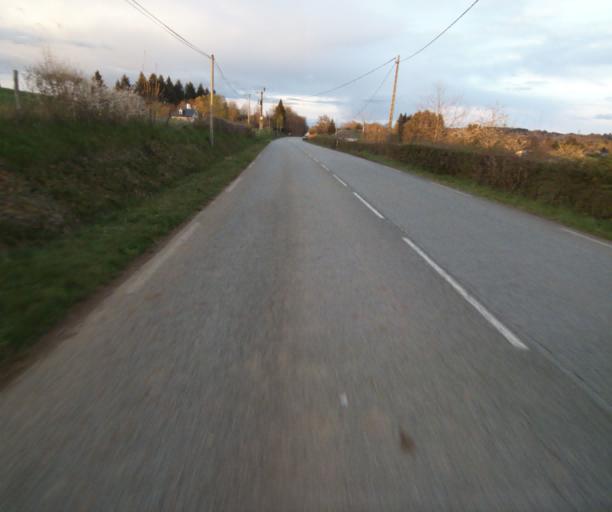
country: FR
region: Limousin
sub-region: Departement de la Correze
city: Laguenne
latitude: 45.2772
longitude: 1.8261
